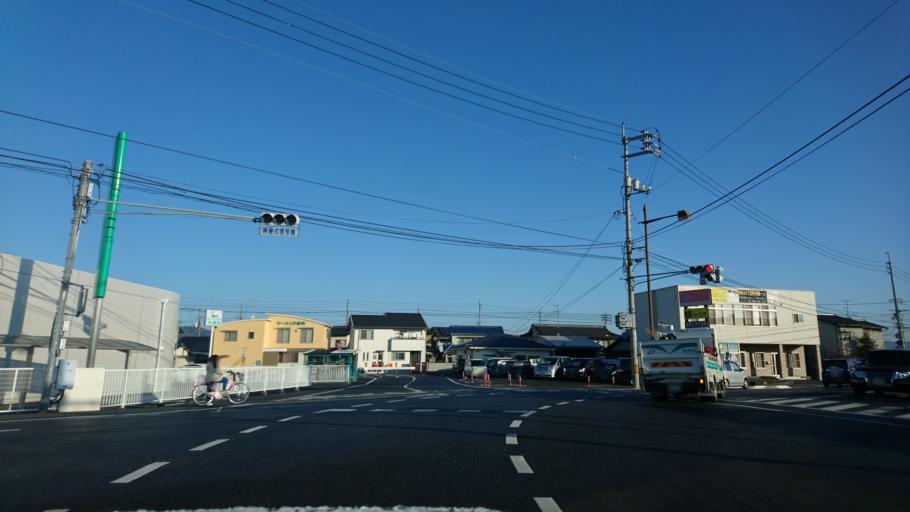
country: JP
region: Okayama
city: Kurashiki
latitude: 34.6036
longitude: 133.7513
